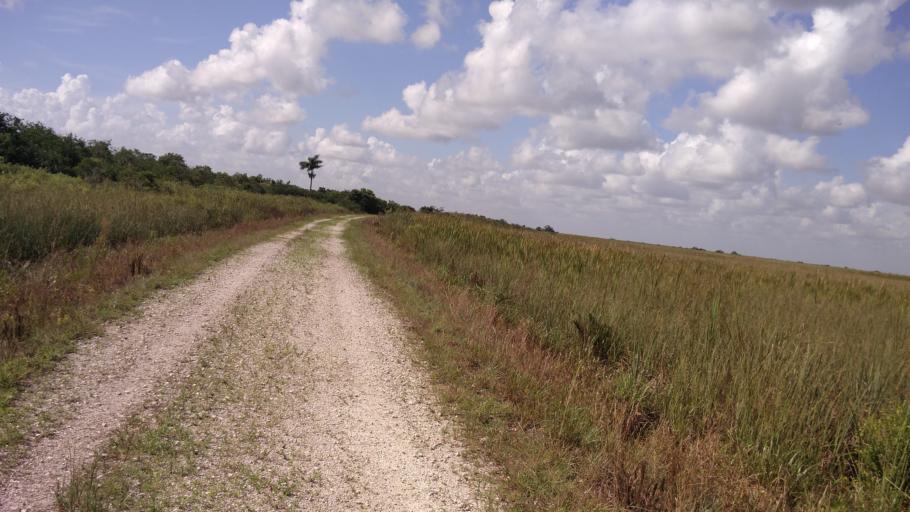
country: US
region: Florida
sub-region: Broward County
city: Weston
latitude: 26.0519
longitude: -80.4616
